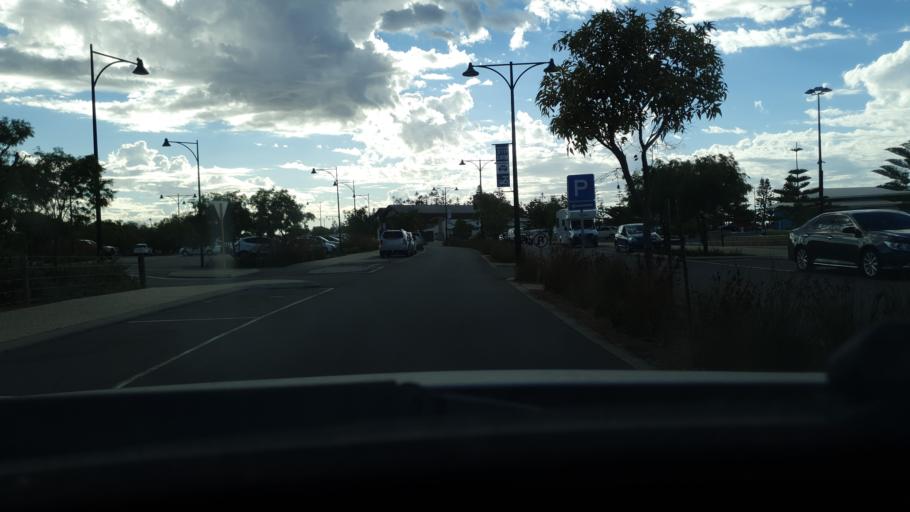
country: AU
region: Western Australia
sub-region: Busselton
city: Busselton
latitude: -33.6451
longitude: 115.3477
